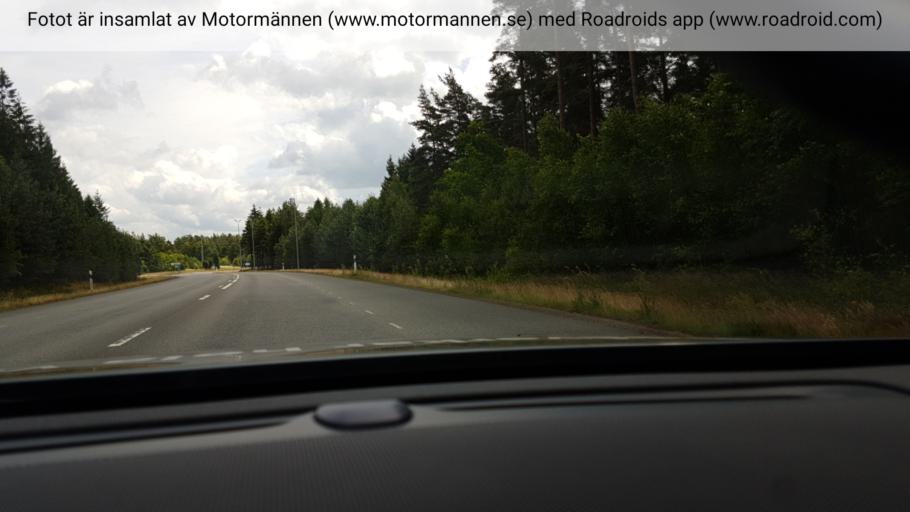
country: SE
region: Skane
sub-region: Hassleholms Kommun
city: Hassleholm
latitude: 56.1698
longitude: 13.8308
